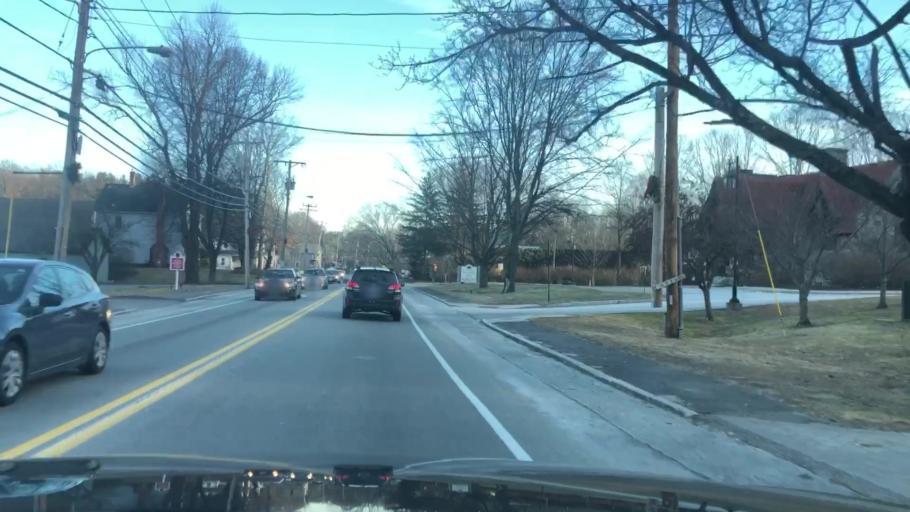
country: US
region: Massachusetts
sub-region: Worcester County
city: Bolton
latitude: 42.4351
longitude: -71.6119
